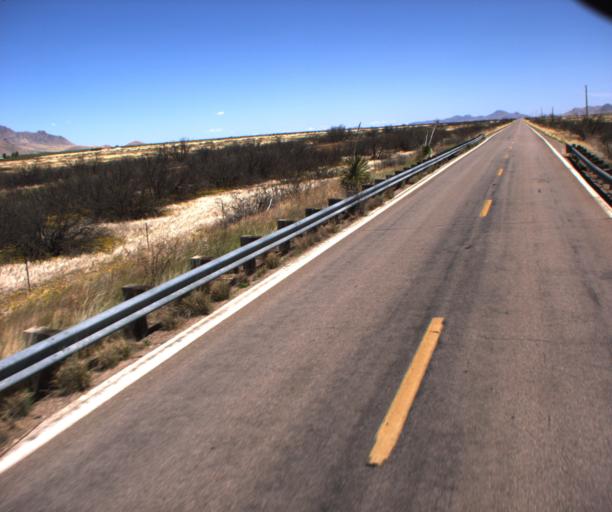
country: US
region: Arizona
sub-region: Cochise County
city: Douglas
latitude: 31.7401
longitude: -109.0983
